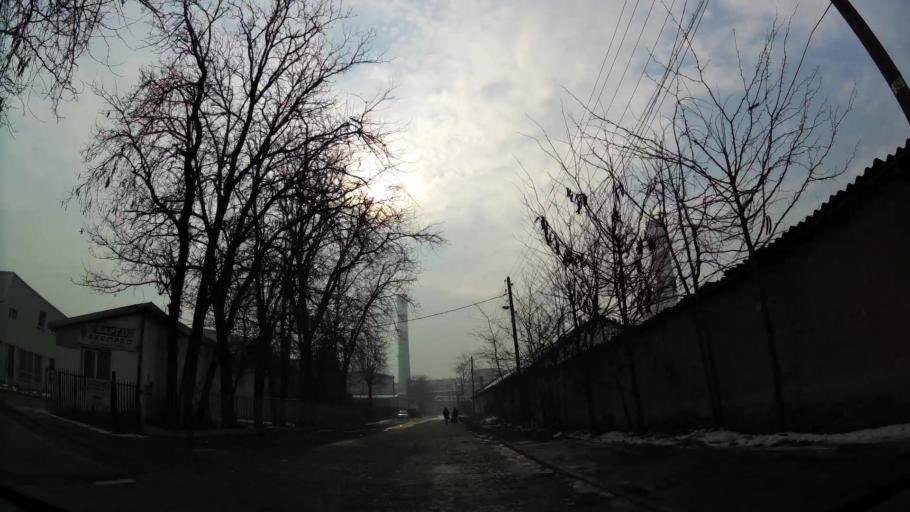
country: MK
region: Karpos
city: Skopje
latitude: 41.9959
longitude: 21.4538
